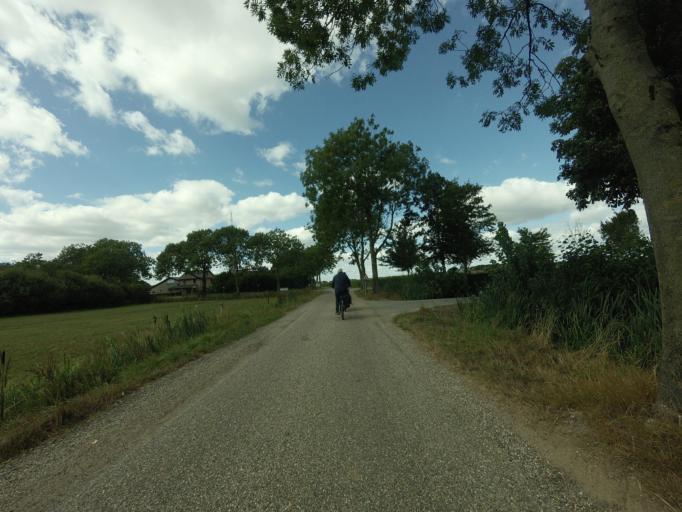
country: NL
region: North Brabant
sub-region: Gemeente Oss
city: Berghem
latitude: 51.8110
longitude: 5.6026
